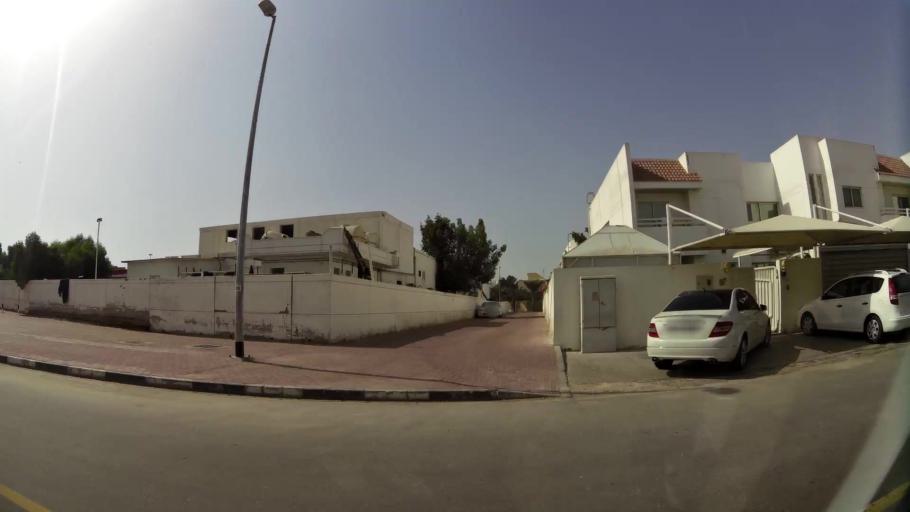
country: AE
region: Ash Shariqah
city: Sharjah
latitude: 25.2416
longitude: 55.3461
